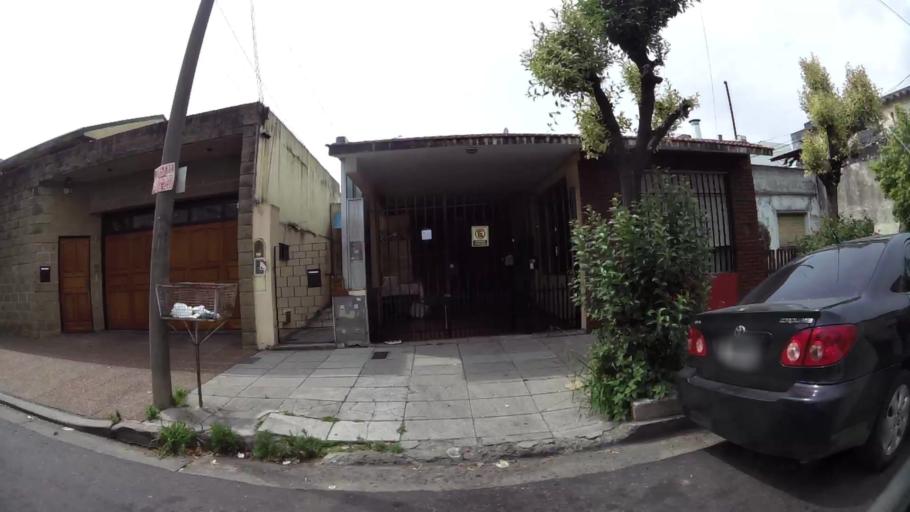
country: AR
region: Buenos Aires F.D.
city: Villa Lugano
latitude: -34.6941
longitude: -58.5115
